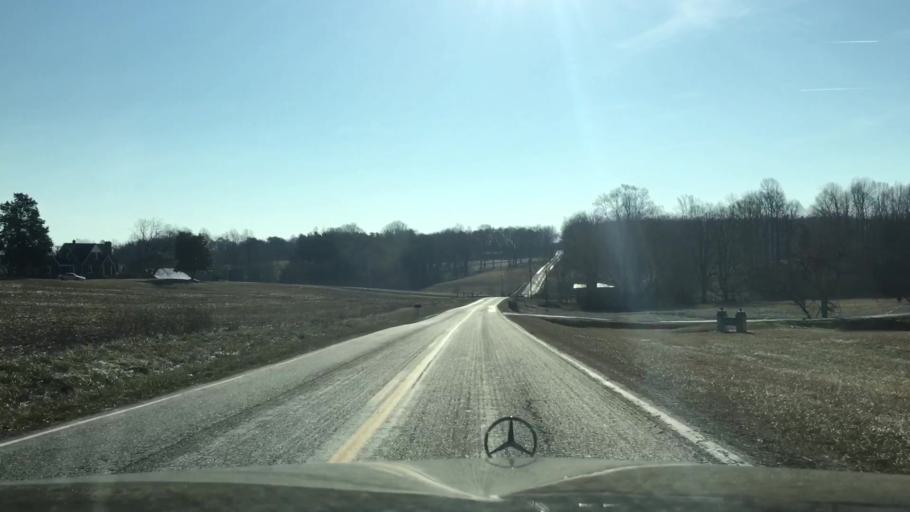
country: US
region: Virginia
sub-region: Pittsylvania County
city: Motley
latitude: 37.1901
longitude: -79.4231
